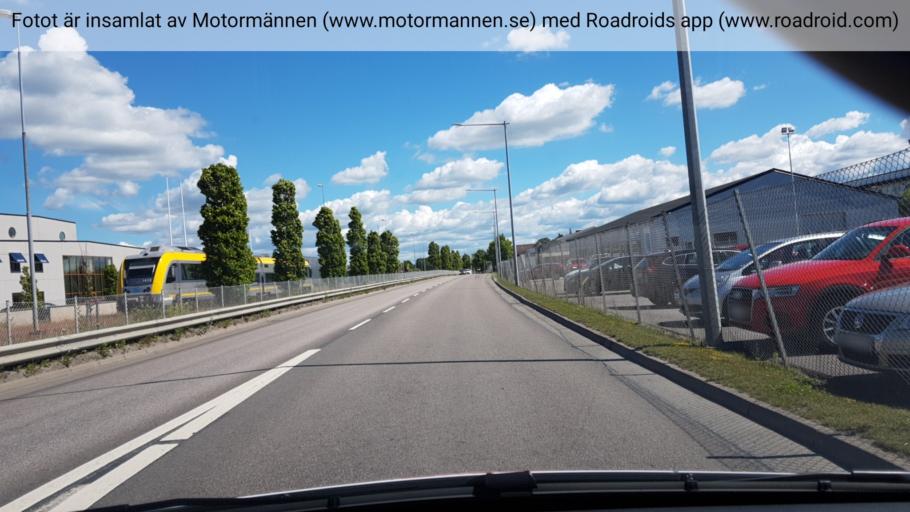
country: SE
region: Vaestra Goetaland
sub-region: Lidkopings Kommun
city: Lidkoping
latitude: 58.5025
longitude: 13.1718
